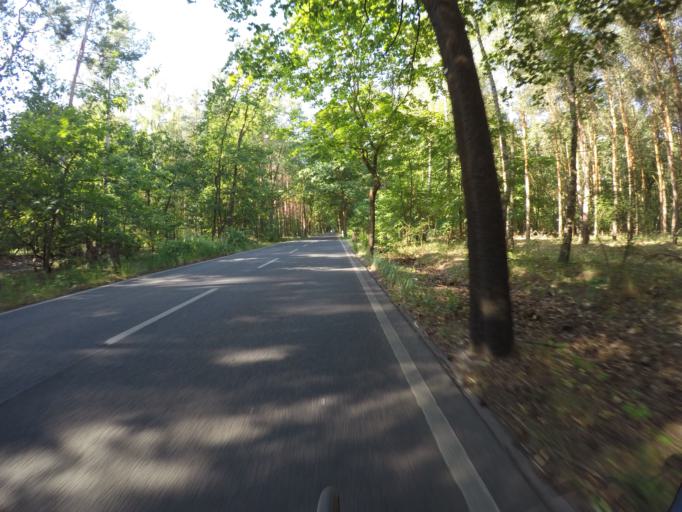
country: DE
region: Berlin
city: Schmockwitz
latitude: 52.3536
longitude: 13.6484
